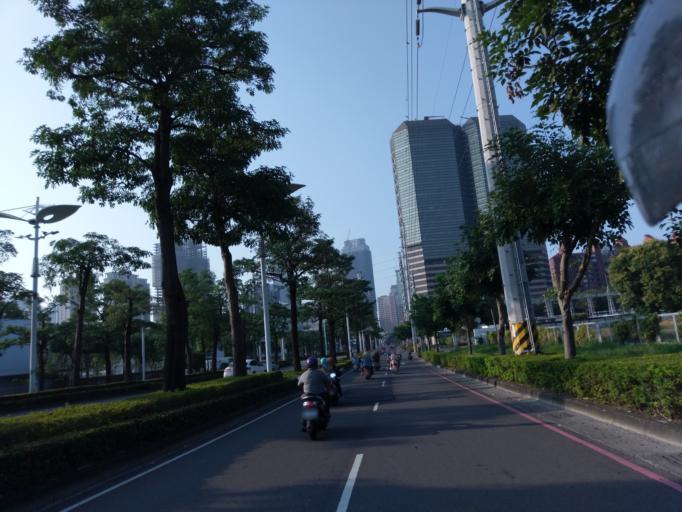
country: TW
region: Kaohsiung
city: Kaohsiung
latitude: 22.6027
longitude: 120.3110
